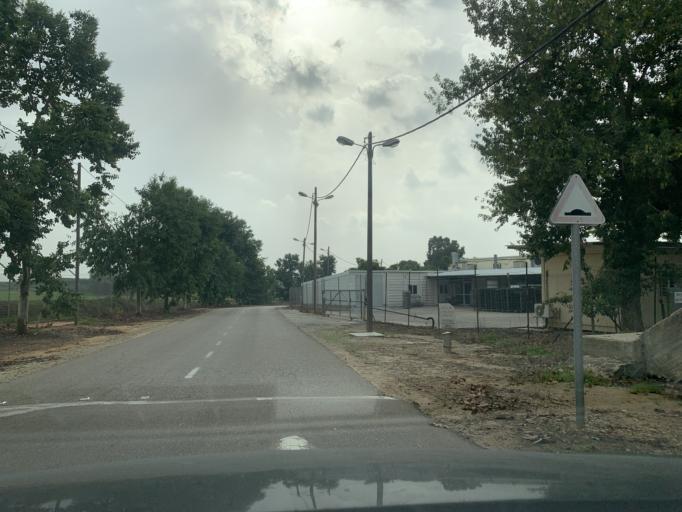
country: IL
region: Central District
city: Tirah
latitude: 32.2156
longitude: 34.9412
